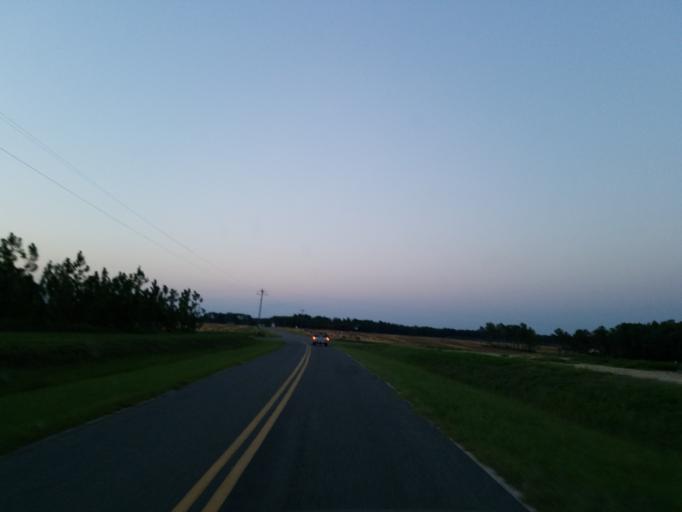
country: US
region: Georgia
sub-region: Dooly County
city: Unadilla
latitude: 32.2893
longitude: -83.7914
